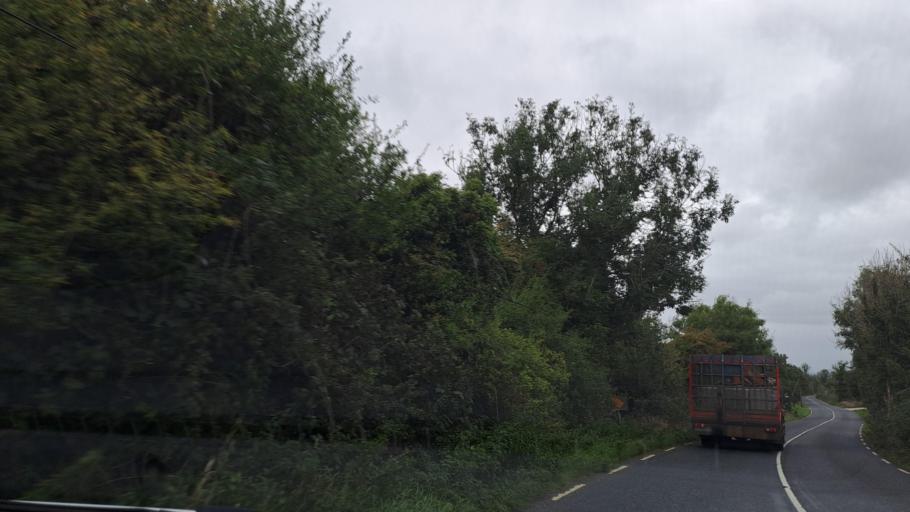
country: IE
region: Ulster
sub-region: County Monaghan
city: Castleblayney
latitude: 54.0932
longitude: -6.8432
